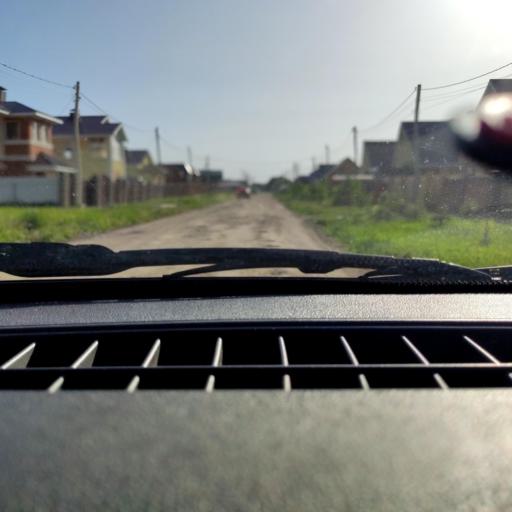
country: RU
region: Bashkortostan
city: Iglino
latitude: 54.8215
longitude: 56.4317
